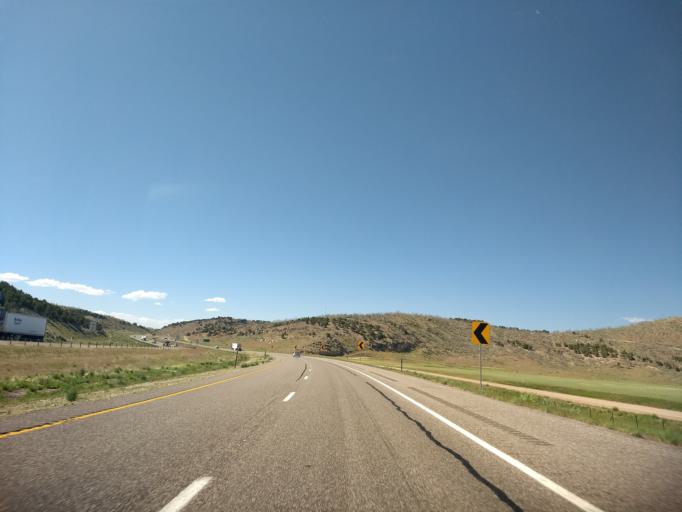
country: US
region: Utah
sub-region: Beaver County
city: Beaver
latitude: 38.6713
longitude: -112.5885
